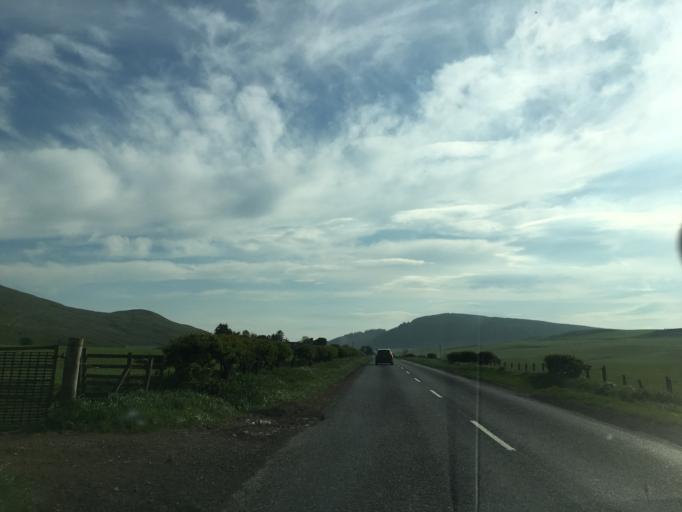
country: GB
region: Scotland
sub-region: The Scottish Borders
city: West Linton
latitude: 55.6766
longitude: -3.4076
